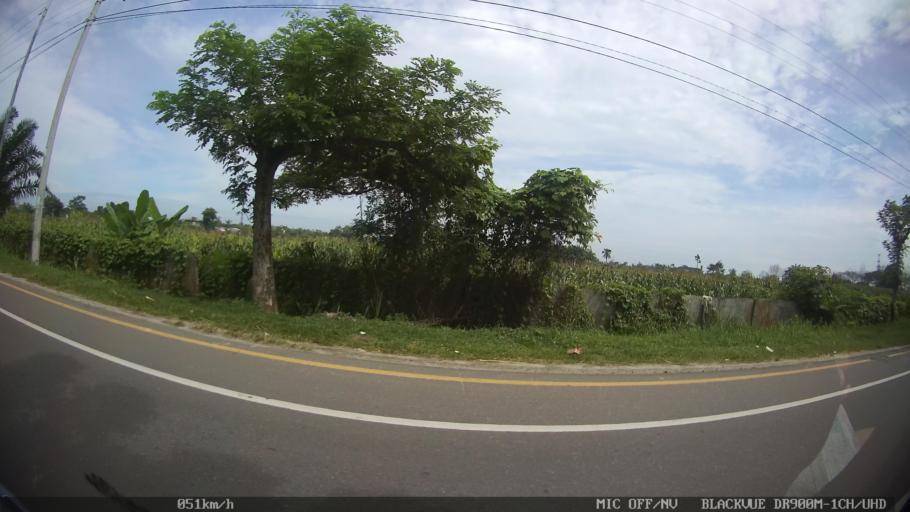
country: ID
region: North Sumatra
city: Percut
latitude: 3.5975
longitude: 98.8097
